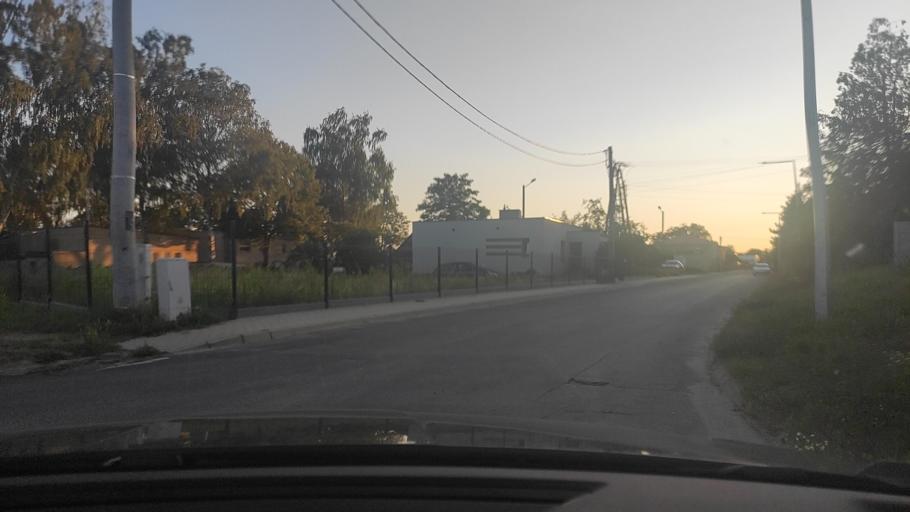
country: PL
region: Greater Poland Voivodeship
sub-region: Powiat poznanski
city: Swarzedz
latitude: 52.4265
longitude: 17.1104
